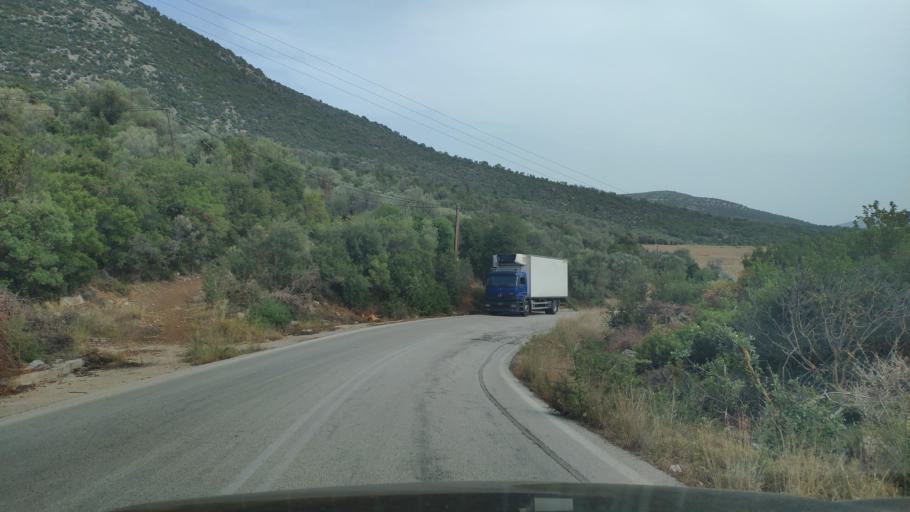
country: GR
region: Peloponnese
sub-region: Nomos Argolidos
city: Palaia Epidavros
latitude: 37.5823
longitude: 23.1540
